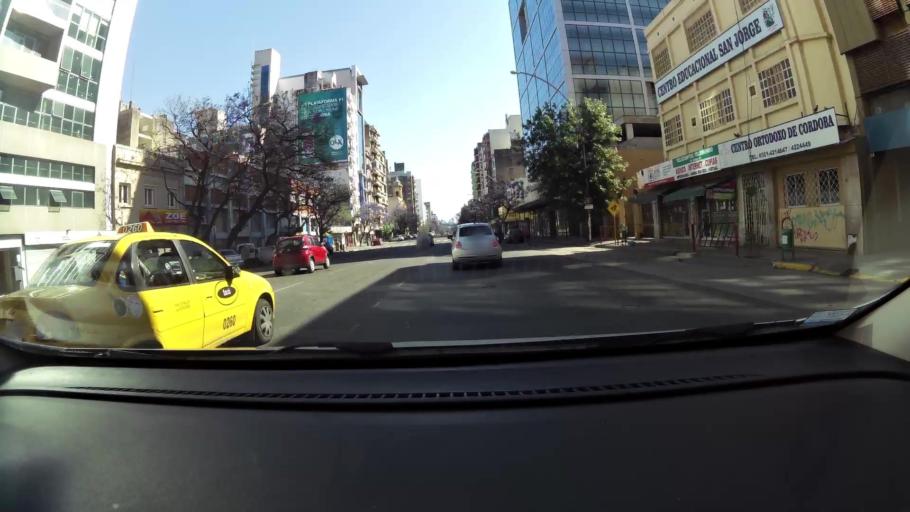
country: AR
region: Cordoba
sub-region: Departamento de Capital
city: Cordoba
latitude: -31.4165
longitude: -64.1799
